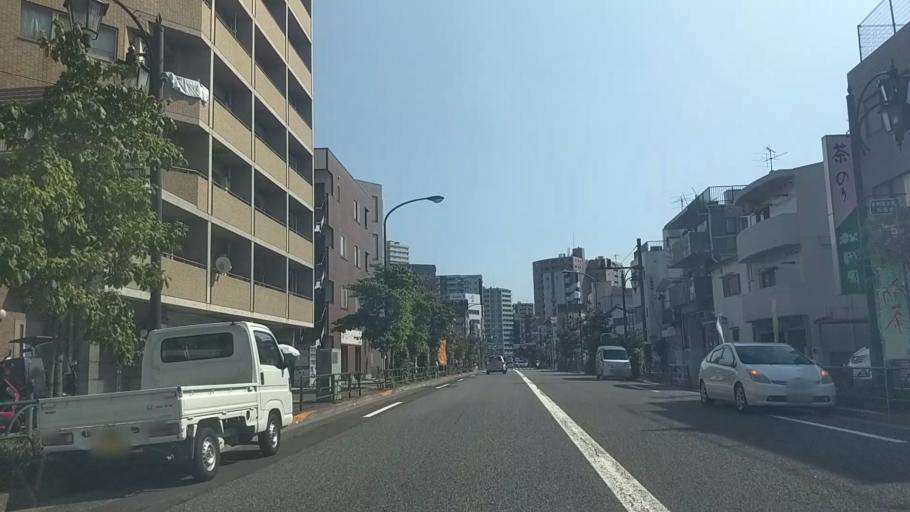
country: JP
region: Kanagawa
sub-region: Kawasaki-shi
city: Kawasaki
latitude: 35.5652
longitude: 139.7221
